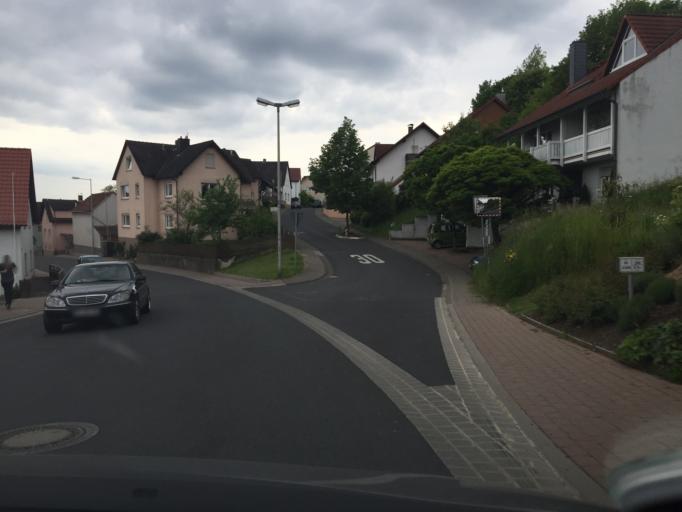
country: DE
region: Bavaria
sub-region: Regierungsbezirk Unterfranken
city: Johannesberg
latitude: 50.0291
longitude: 9.1371
